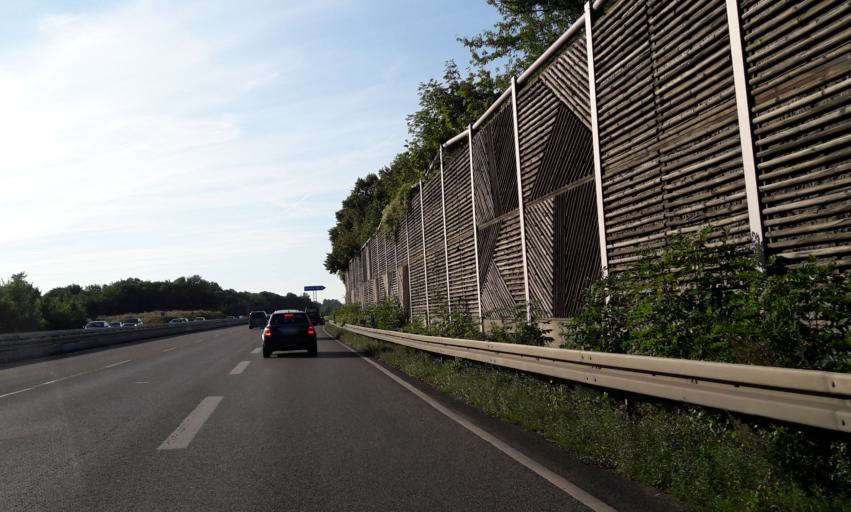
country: DE
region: Baden-Wuerttemberg
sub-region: Regierungsbezirk Stuttgart
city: Korntal
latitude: 48.8485
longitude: 9.1253
